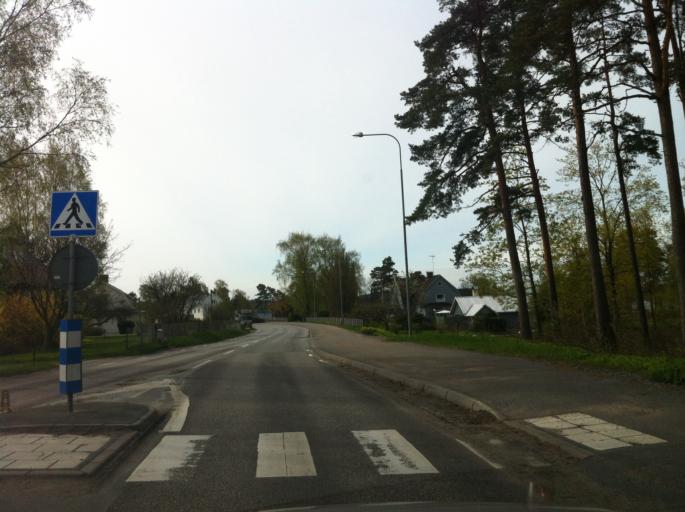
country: SE
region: Vaestra Goetaland
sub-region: Marks Kommun
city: Kinna
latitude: 57.4766
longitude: 12.7050
